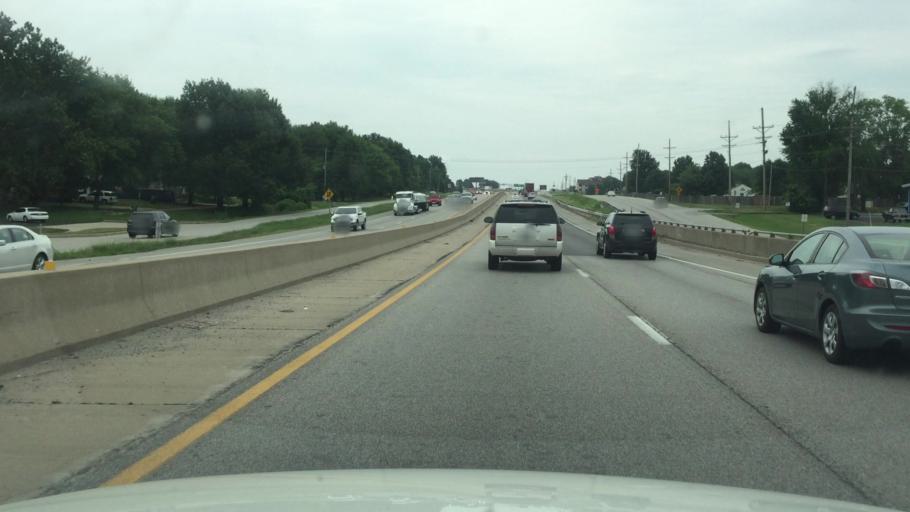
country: US
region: Missouri
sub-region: Jackson County
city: Lees Summit
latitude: 38.9088
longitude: -94.3901
